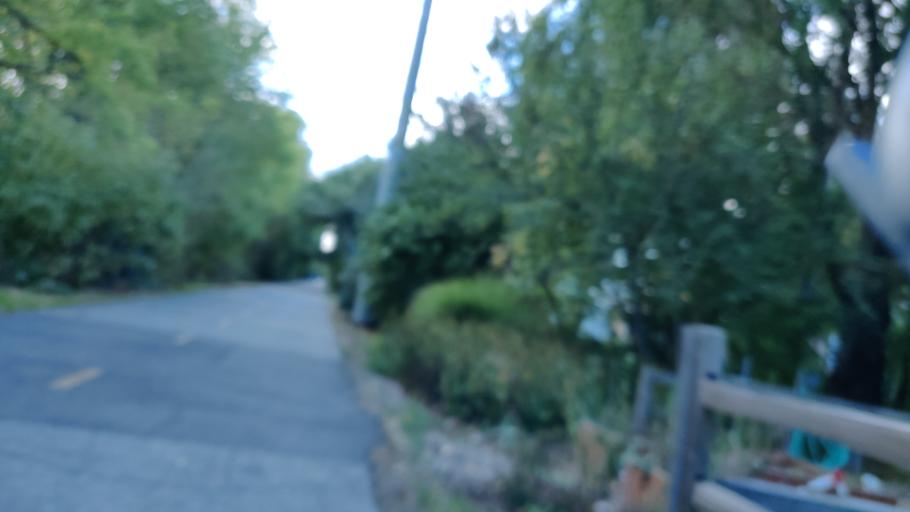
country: US
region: Idaho
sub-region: Ada County
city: Boise
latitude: 43.6012
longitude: -116.1781
